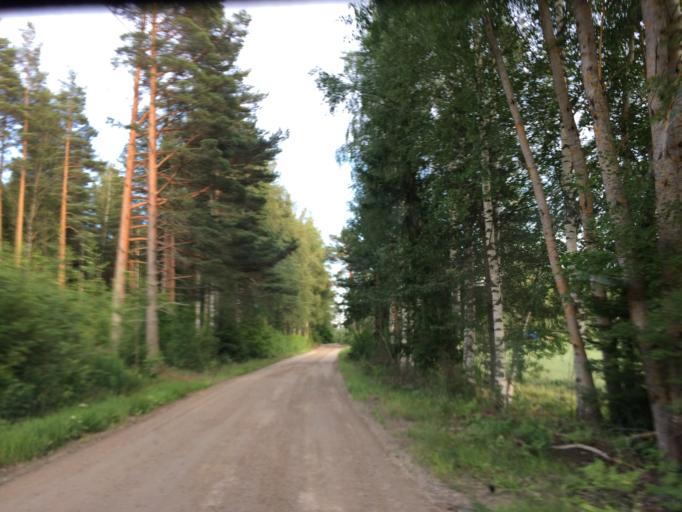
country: FI
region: Haeme
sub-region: Haemeenlinna
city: Janakkala
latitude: 60.8907
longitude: 24.6028
